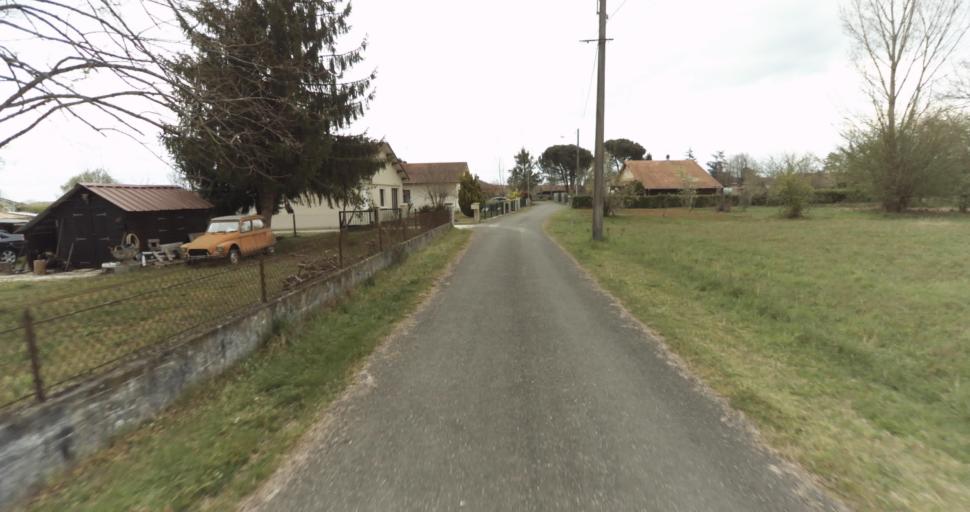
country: FR
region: Aquitaine
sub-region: Departement des Landes
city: Roquefort
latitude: 44.0242
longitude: -0.3284
